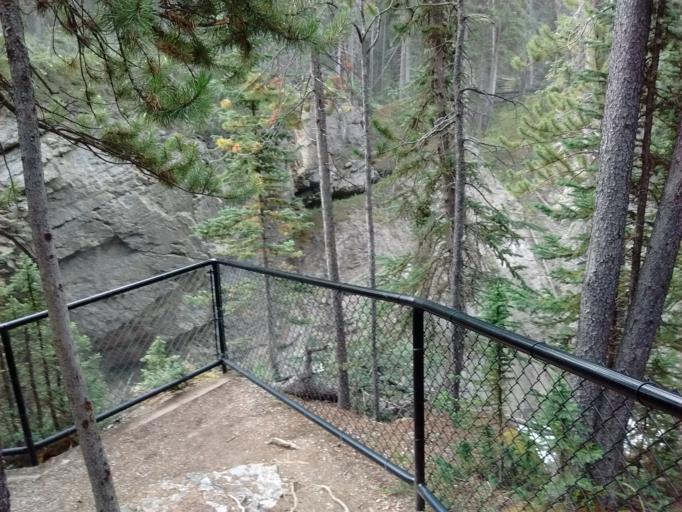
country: CA
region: Alberta
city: Jasper Park Lodge
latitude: 52.5250
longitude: -117.6568
